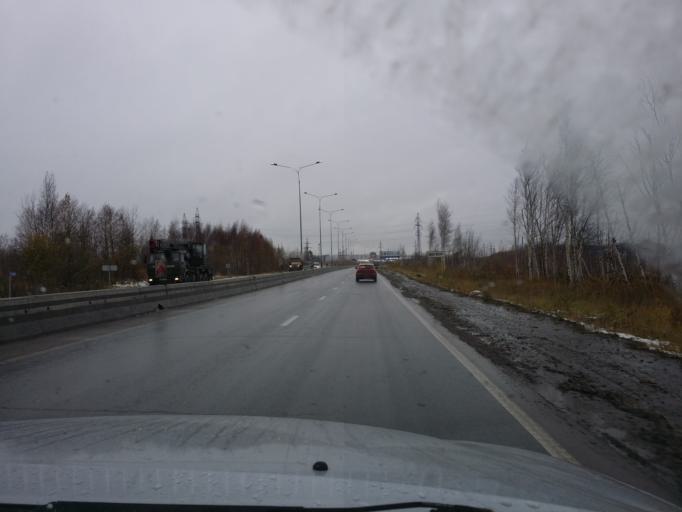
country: RU
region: Khanty-Mansiyskiy Avtonomnyy Okrug
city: Megion
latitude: 61.0501
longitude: 76.1356
